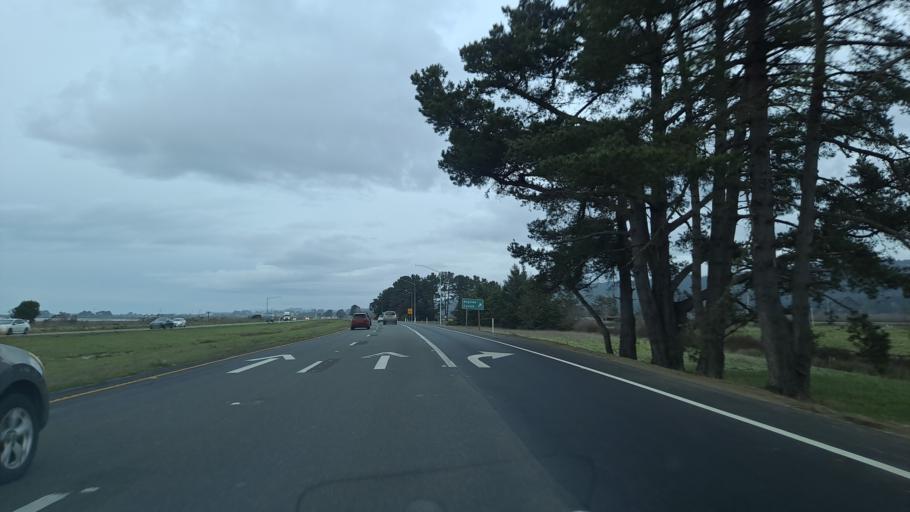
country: US
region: California
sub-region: Humboldt County
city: Bayside
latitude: 40.8321
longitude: -124.0820
